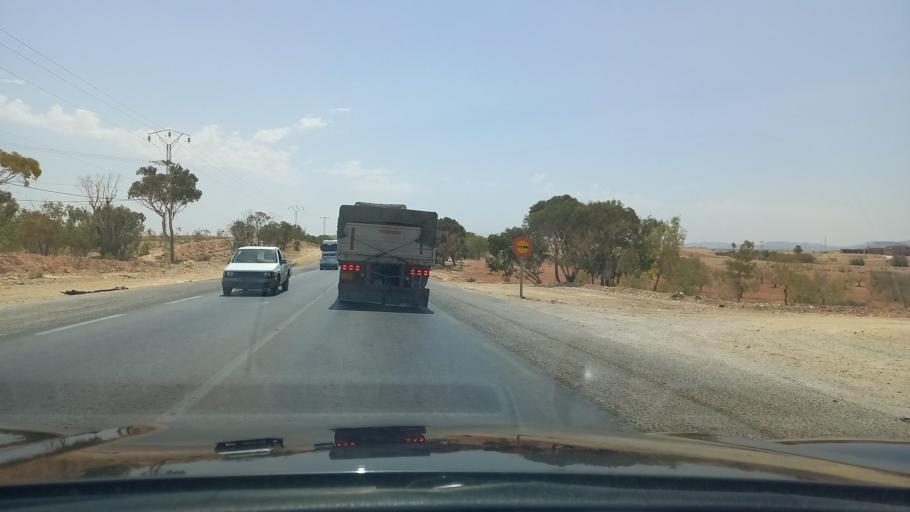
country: TN
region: Madanin
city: Medenine
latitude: 33.5690
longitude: 10.3171
